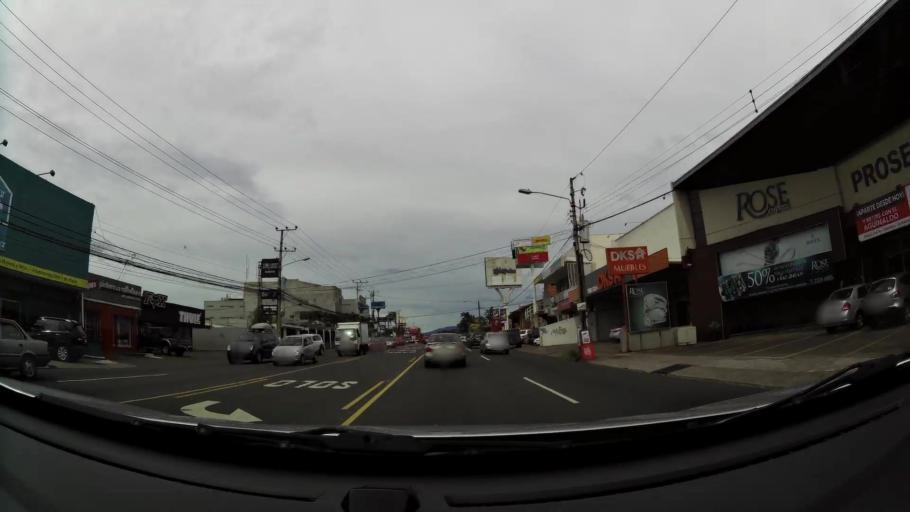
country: CR
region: San Jose
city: San Pedro
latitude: 9.9269
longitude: -84.0409
